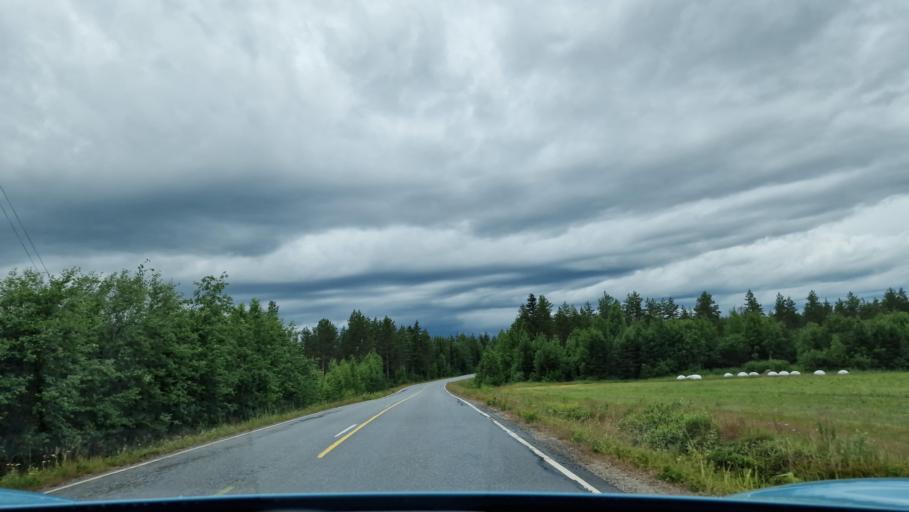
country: FI
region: Southern Ostrobothnia
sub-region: Jaerviseutu
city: Soini
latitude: 62.6836
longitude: 24.4729
